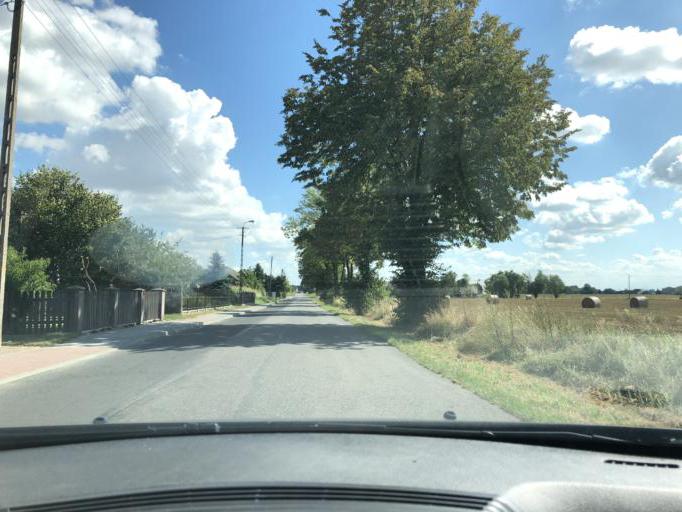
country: PL
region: Lodz Voivodeship
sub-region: Powiat wieruszowski
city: Czastary
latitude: 51.2589
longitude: 18.3265
